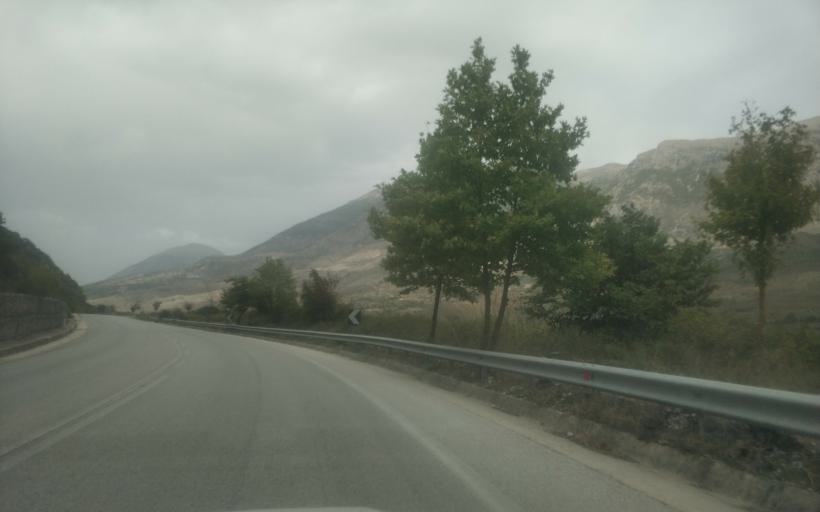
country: AL
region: Gjirokaster
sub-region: Rrethi i Gjirokastres
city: Picar
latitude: 40.2216
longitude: 20.0876
